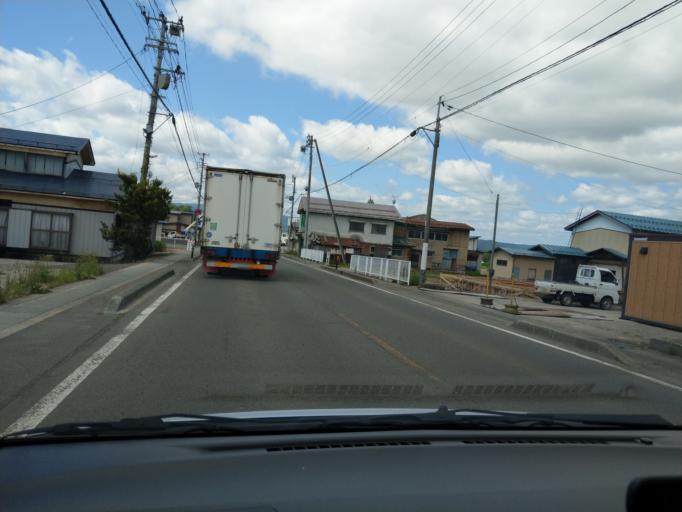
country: JP
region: Akita
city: Yuzawa
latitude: 39.1832
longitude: 140.4976
